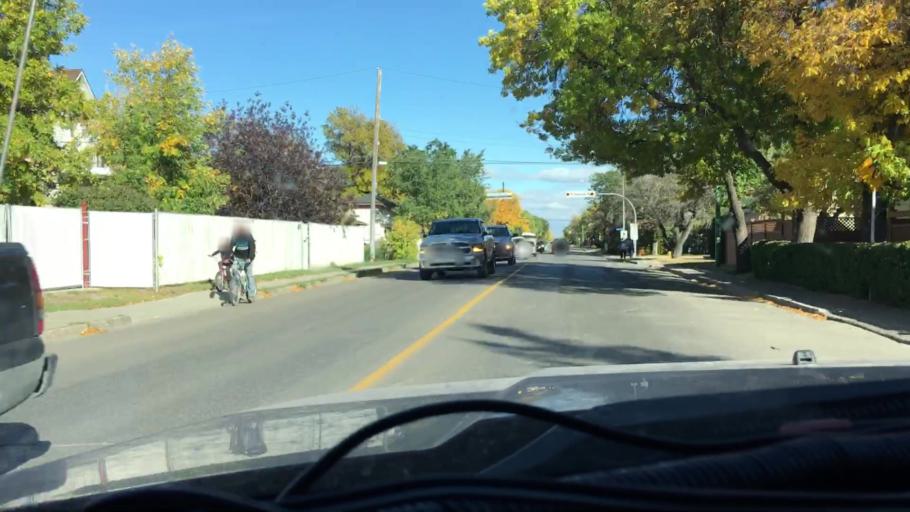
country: CA
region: Saskatchewan
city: Regina
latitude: 50.4629
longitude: -104.6296
